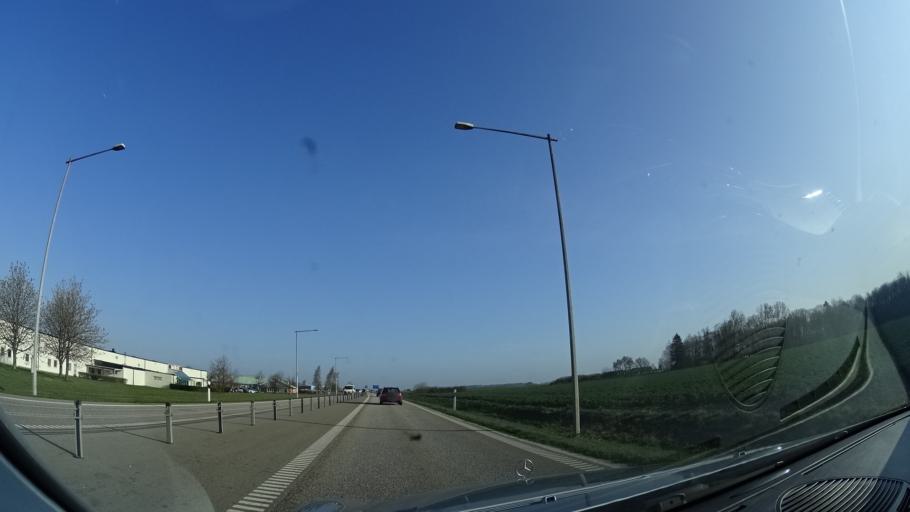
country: SE
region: Skane
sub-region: Eslovs Kommun
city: Eslov
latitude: 55.8365
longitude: 13.3304
